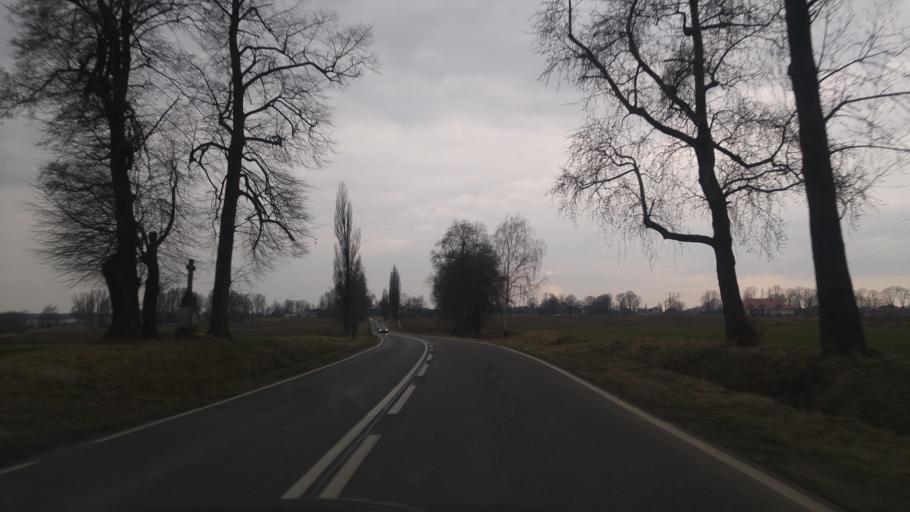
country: PL
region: Silesian Voivodeship
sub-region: Powiat pszczynski
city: Radostowice
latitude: 49.9514
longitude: 18.8643
